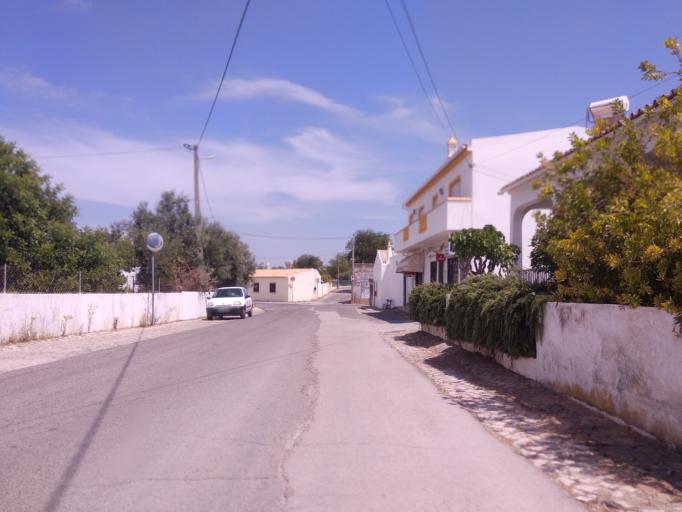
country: PT
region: Faro
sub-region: Faro
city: Santa Barbara de Nexe
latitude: 37.1212
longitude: -7.9430
